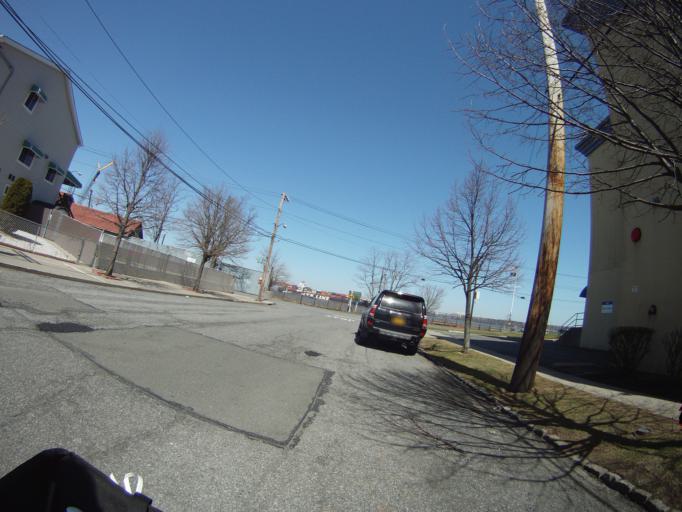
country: US
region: New York
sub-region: Kings County
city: Bensonhurst
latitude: 40.6161
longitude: -74.0644
